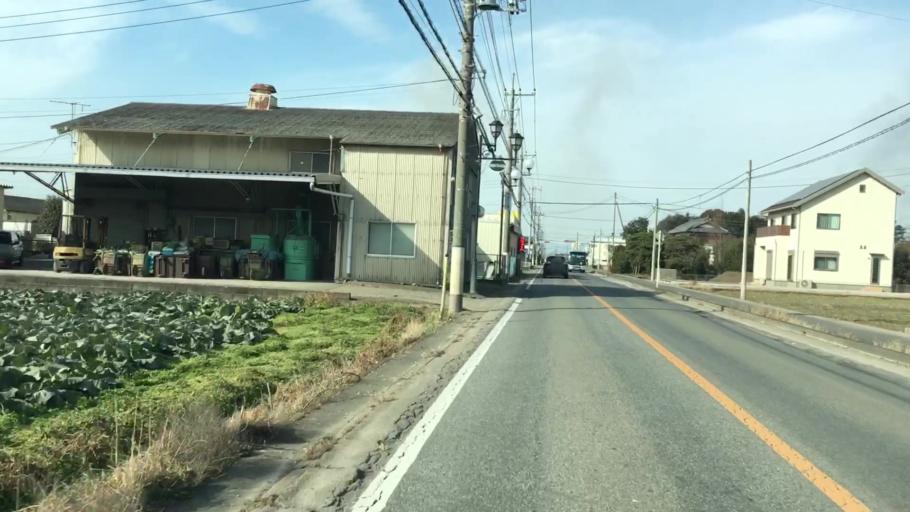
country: JP
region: Saitama
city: Menuma
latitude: 36.2409
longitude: 139.4536
